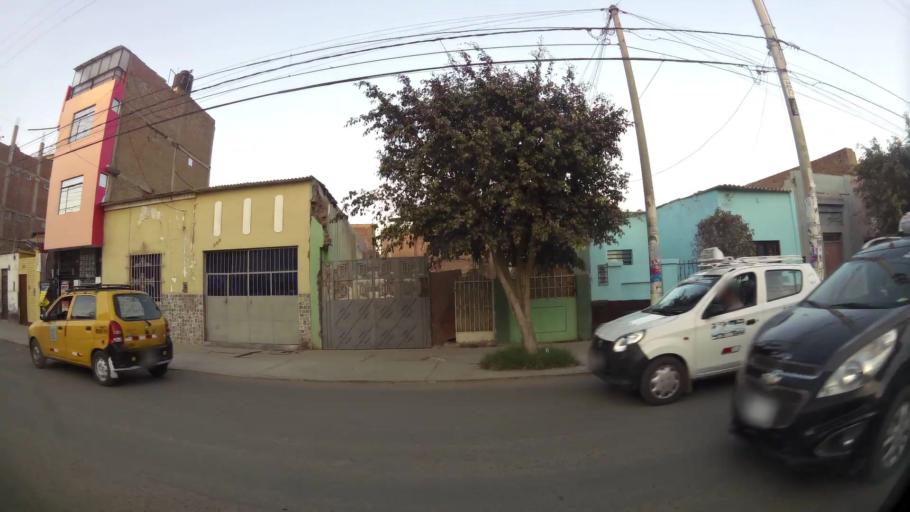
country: PE
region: Lambayeque
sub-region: Provincia de Chiclayo
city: Santa Rosa
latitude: -6.7689
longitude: -79.8328
